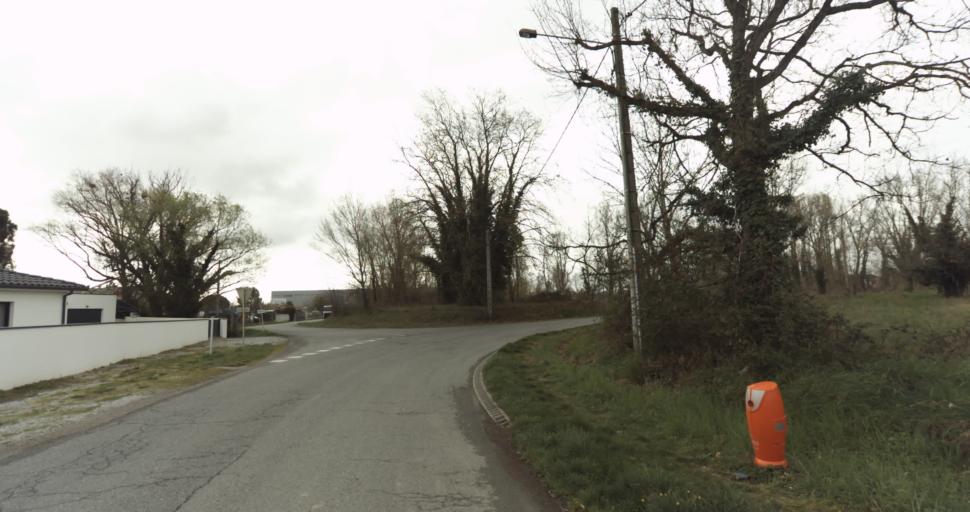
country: FR
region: Midi-Pyrenees
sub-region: Departement de la Haute-Garonne
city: Auterive
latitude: 43.3663
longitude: 1.4597
